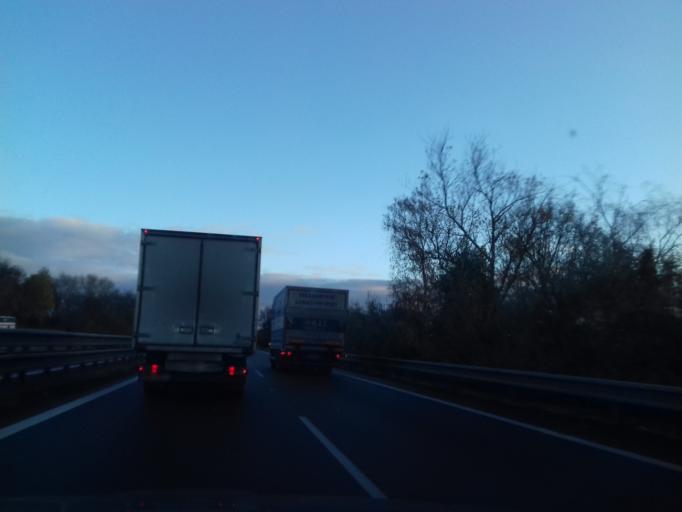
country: CZ
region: South Moravian
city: Pustimer
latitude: 49.3422
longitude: 17.0657
